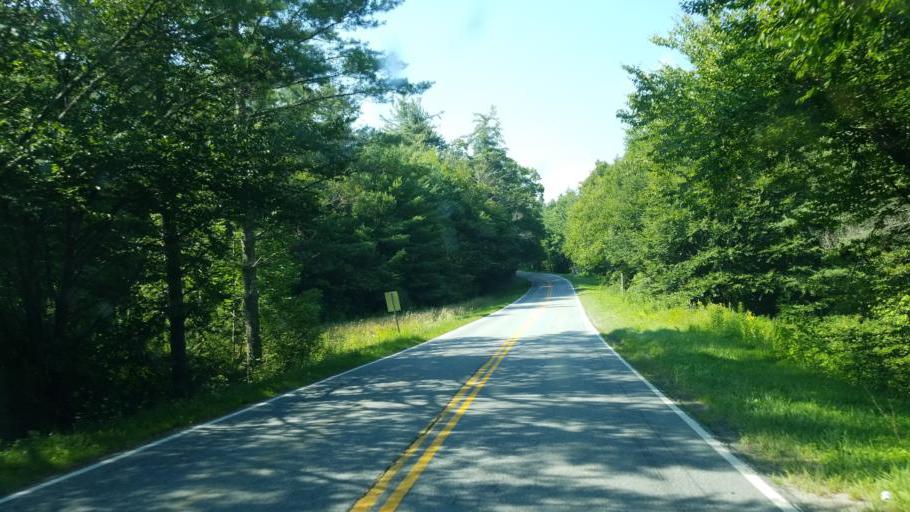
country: US
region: North Carolina
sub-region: Avery County
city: Newland
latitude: 36.0014
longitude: -81.8891
